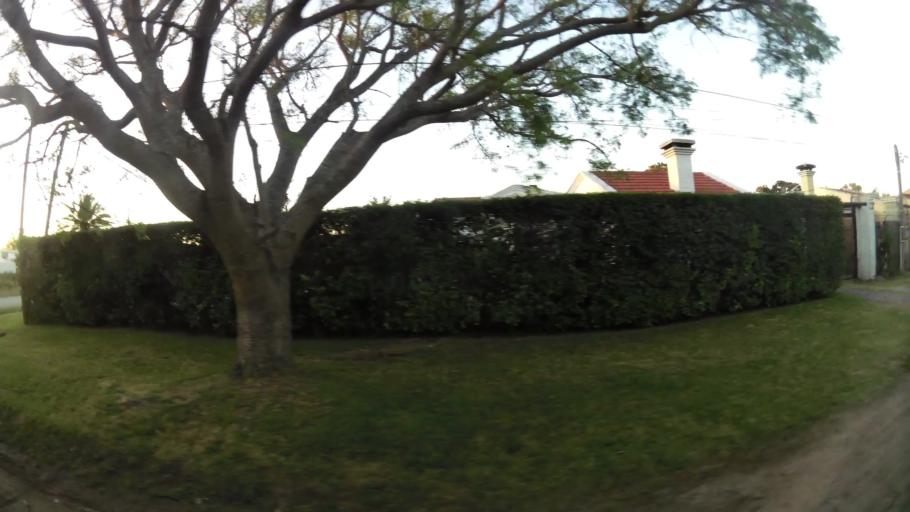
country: UY
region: Canelones
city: Barra de Carrasco
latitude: -34.8490
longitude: -55.9814
